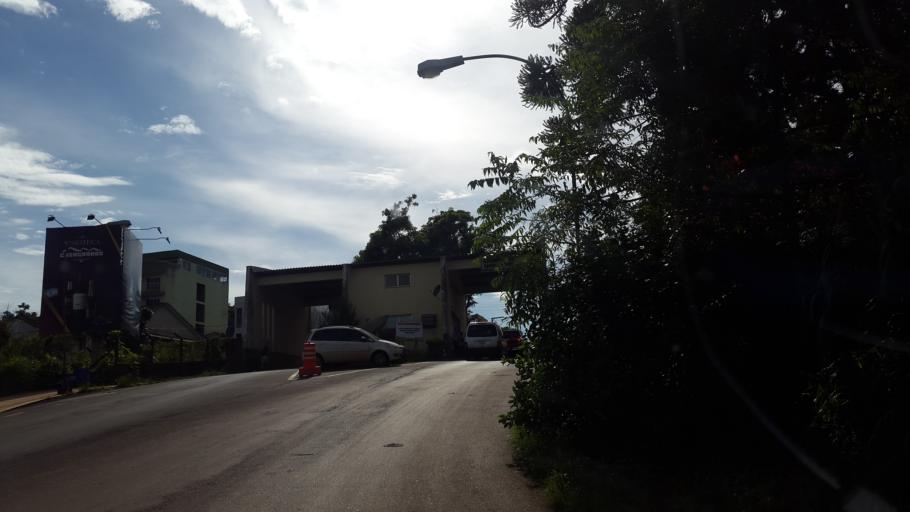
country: AR
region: Misiones
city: Bernardo de Irigoyen
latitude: -26.2548
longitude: -53.6436
